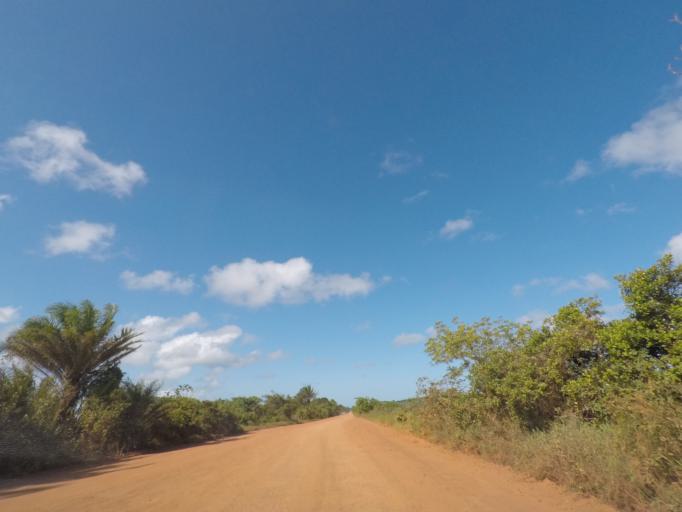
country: BR
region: Bahia
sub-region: Marau
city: Marau
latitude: -14.1535
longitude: -39.0078
